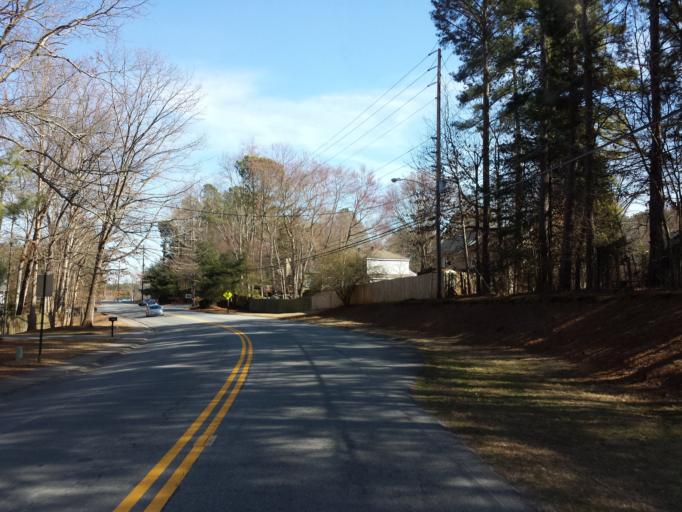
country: US
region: Georgia
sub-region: Cobb County
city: Kennesaw
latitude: 34.0296
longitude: -84.6032
